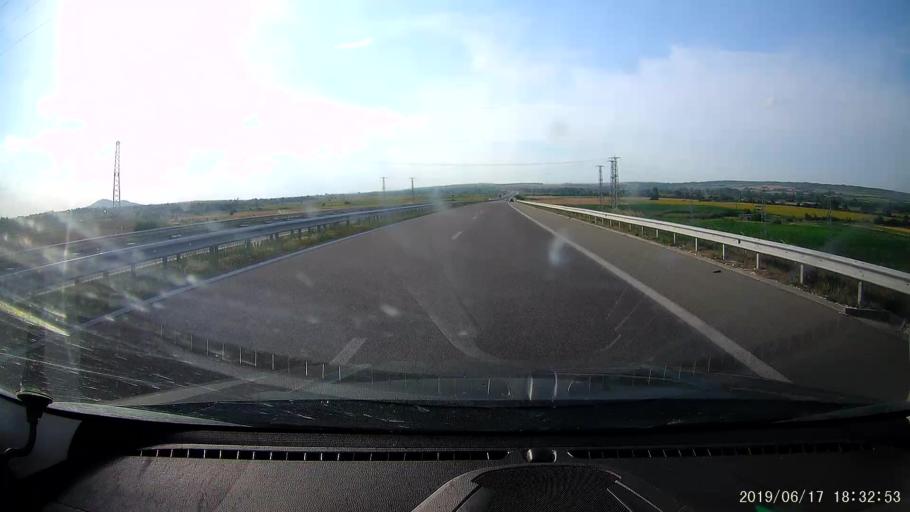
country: BG
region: Khaskovo
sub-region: Obshtina Dimitrovgrad
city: Dimitrovgrad
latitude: 42.0680
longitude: 25.4691
